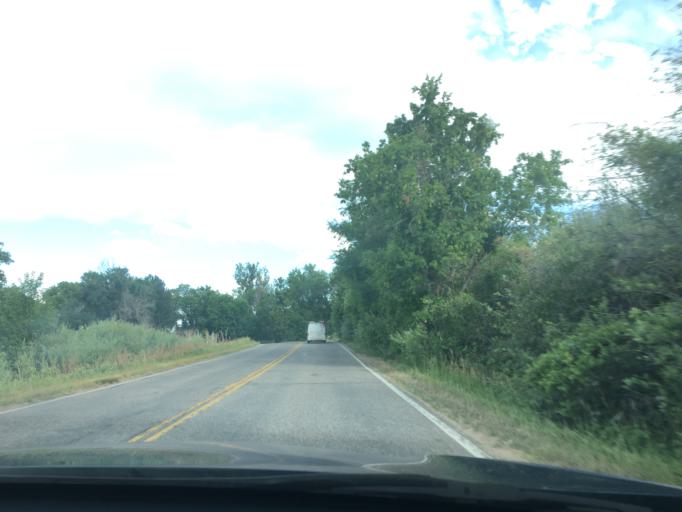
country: US
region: Colorado
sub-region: Jefferson County
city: Applewood
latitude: 39.7624
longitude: -105.1817
